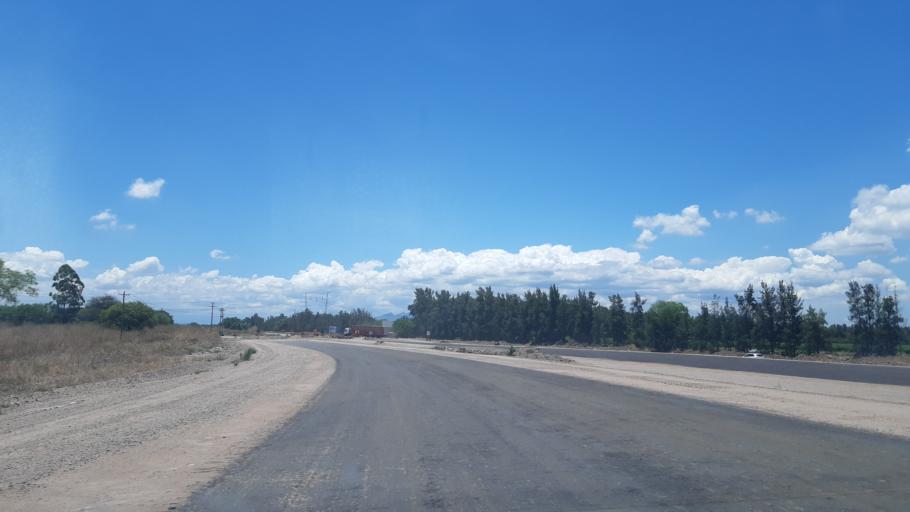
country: AR
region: Jujuy
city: La Mendieta
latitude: -24.4741
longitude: -65.0385
